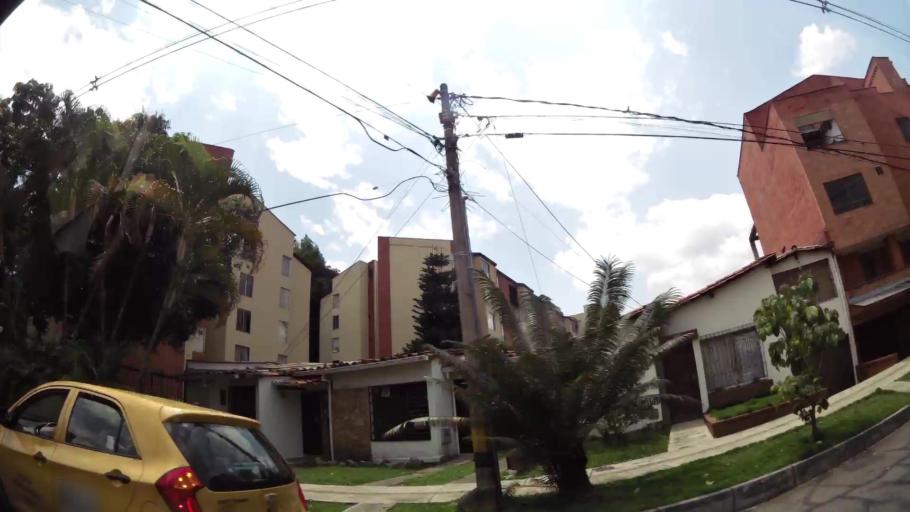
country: CO
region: Antioquia
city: Medellin
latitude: 6.2369
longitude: -75.5995
